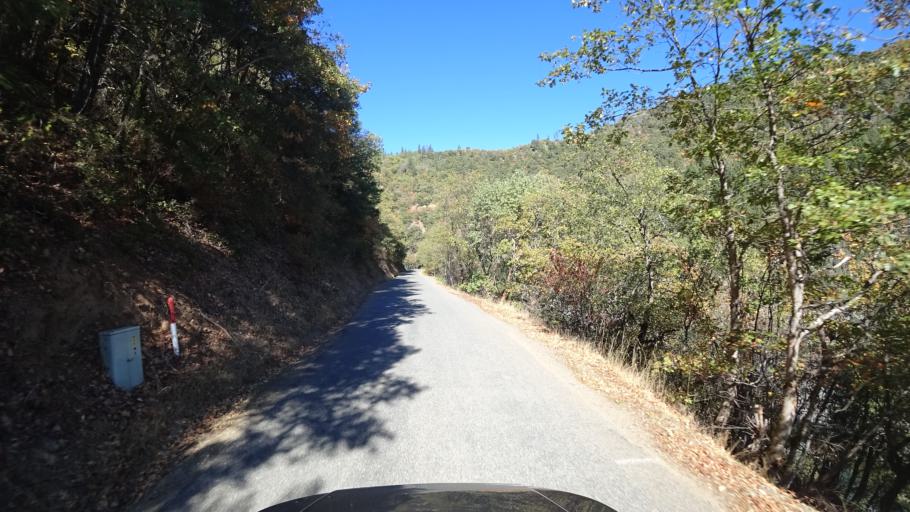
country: US
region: California
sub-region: Humboldt County
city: Willow Creek
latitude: 41.2525
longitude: -123.3075
